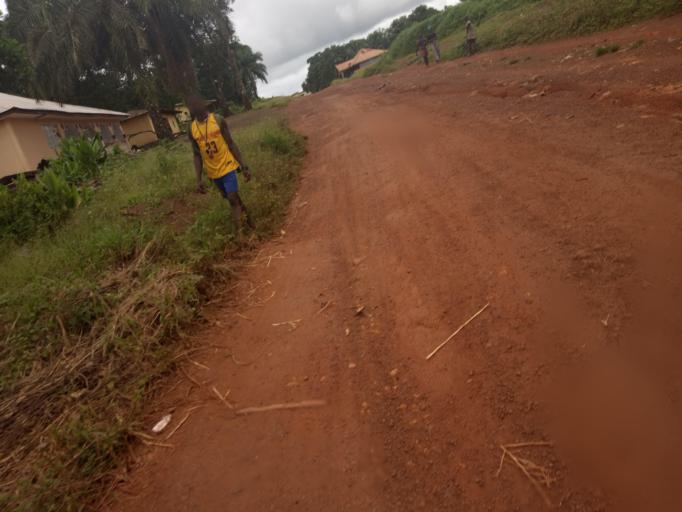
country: SL
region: Northern Province
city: Kamakwie
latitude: 9.4991
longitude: -12.2478
